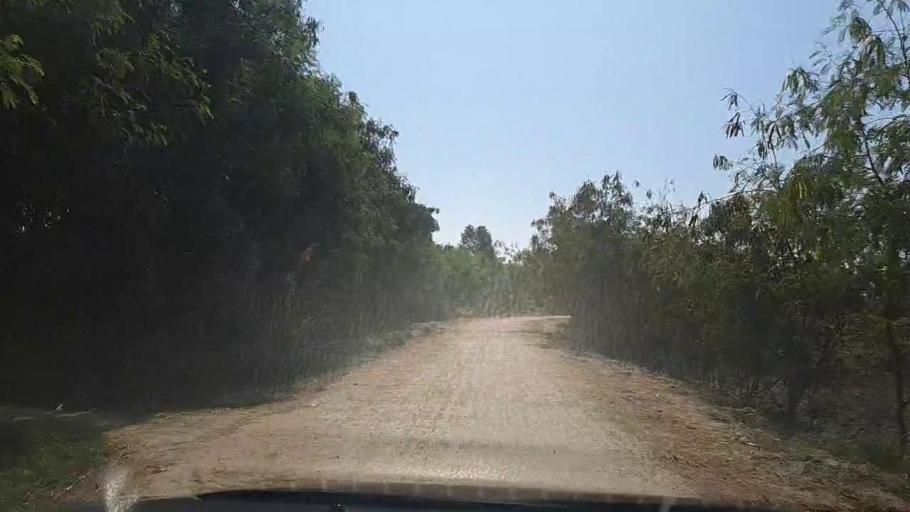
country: PK
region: Sindh
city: Thatta
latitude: 24.5919
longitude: 67.8197
